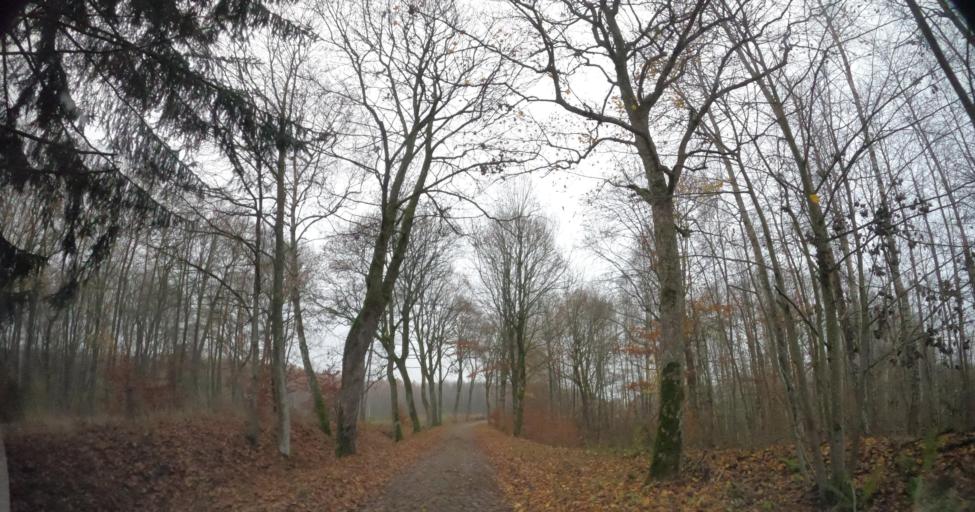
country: PL
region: West Pomeranian Voivodeship
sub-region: Powiat drawski
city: Drawsko Pomorskie
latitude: 53.5610
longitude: 15.7252
